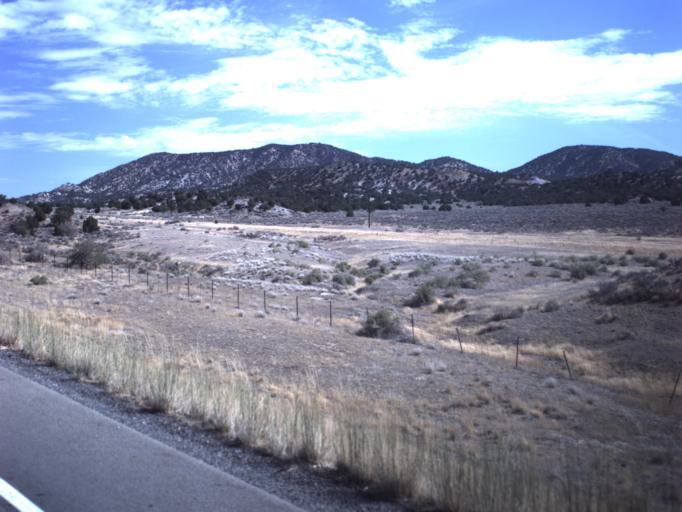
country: US
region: Utah
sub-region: Sanpete County
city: Gunnison
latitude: 39.3816
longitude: -111.9278
